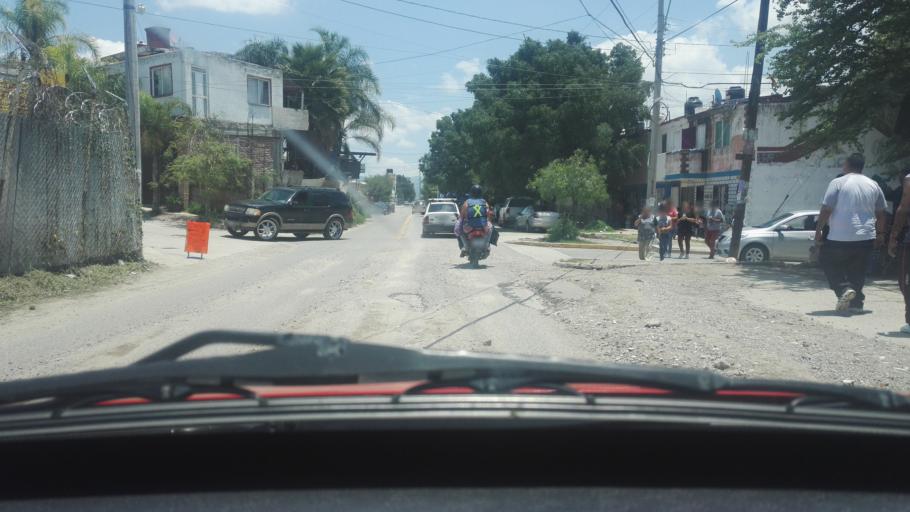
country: MX
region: Guanajuato
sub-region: Leon
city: San Jose de Duran (Los Troncoso)
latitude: 21.0851
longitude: -101.6304
